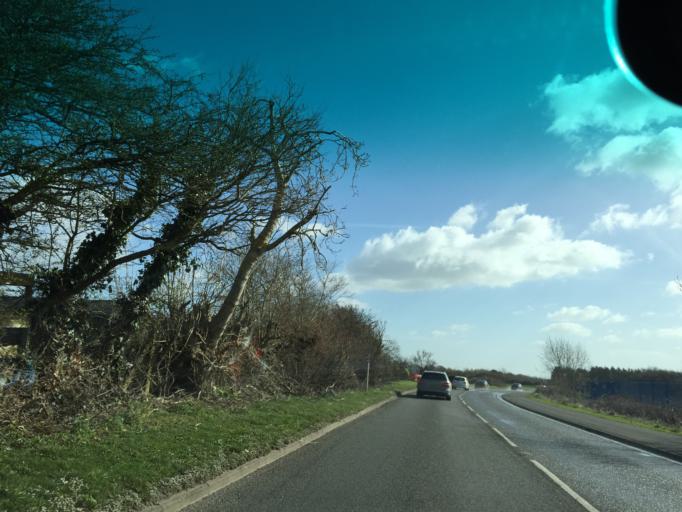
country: GB
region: England
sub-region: Hampshire
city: Lee-on-the-Solent
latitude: 50.8215
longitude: -1.1997
